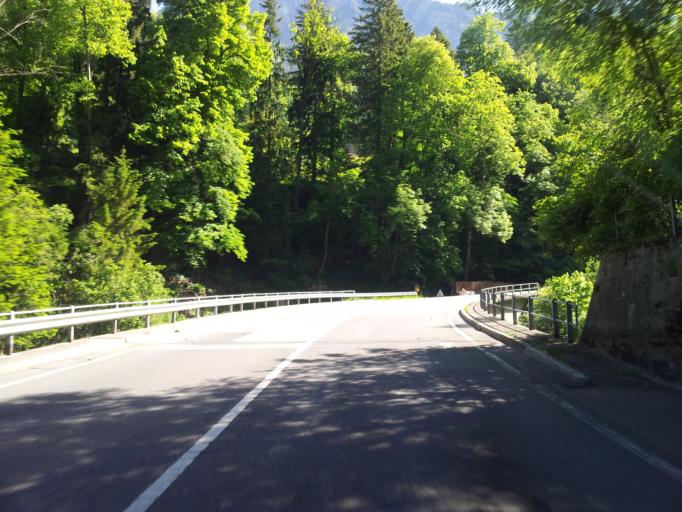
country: CH
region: Bern
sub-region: Interlaken-Oberhasli District
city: Lauterbrunnen
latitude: 46.6366
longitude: 7.9649
